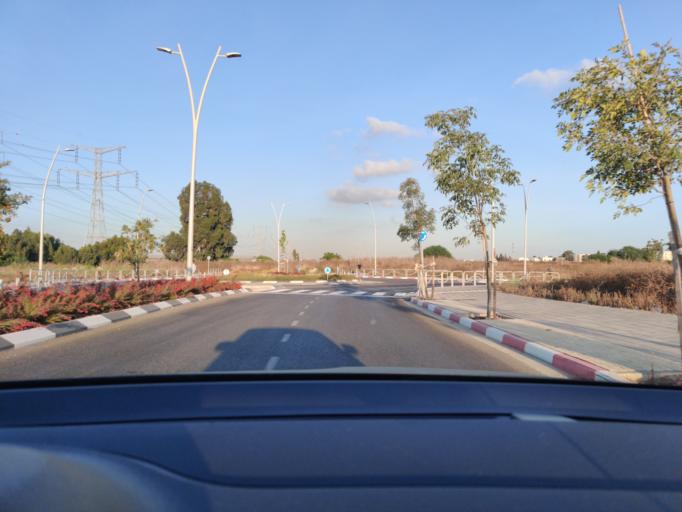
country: IL
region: Central District
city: Elyakhin
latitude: 32.4366
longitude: 34.9442
